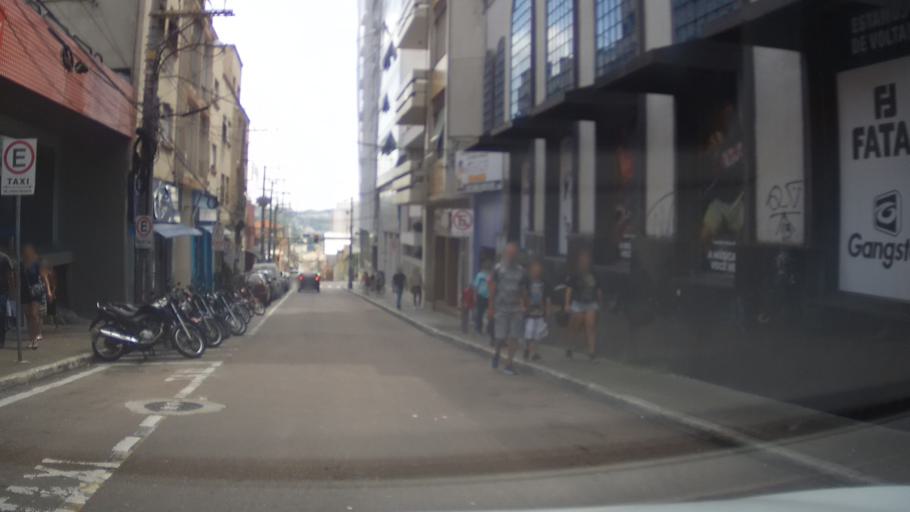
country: BR
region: Sao Paulo
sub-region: Jundiai
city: Jundiai
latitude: -23.1875
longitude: -46.8849
